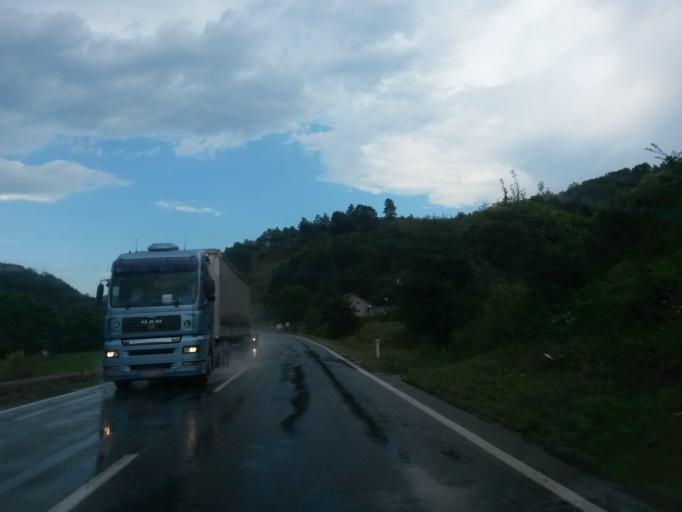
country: BA
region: Federation of Bosnia and Herzegovina
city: Lijesnica
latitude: 44.4968
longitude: 18.0820
